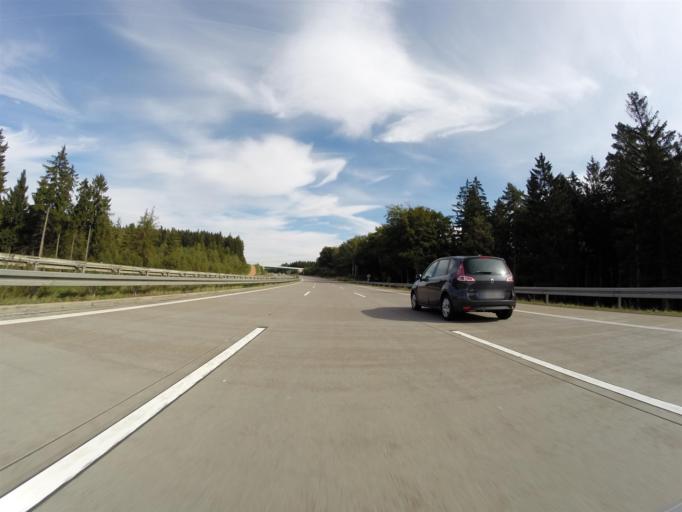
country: DE
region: Saxony
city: Limbach-Oberfrohna
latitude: 50.8308
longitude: 12.7883
